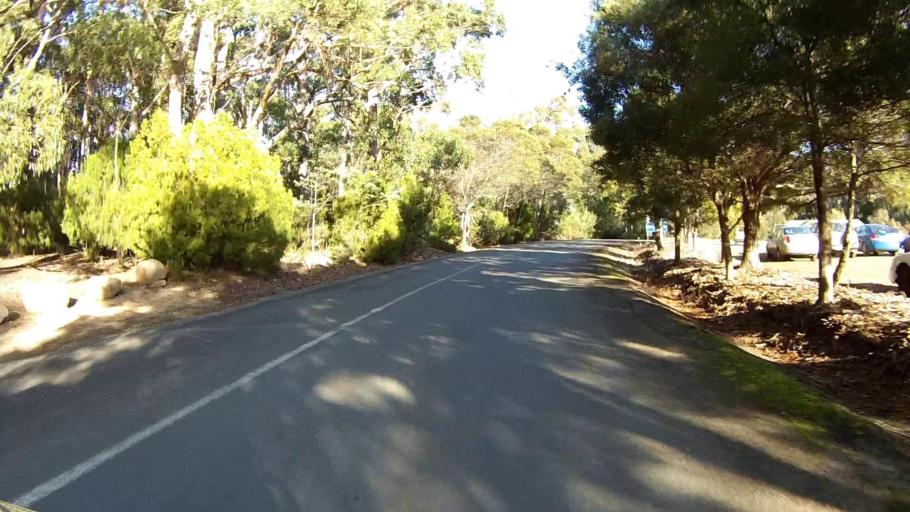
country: AU
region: Tasmania
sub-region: Clarence
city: Sandford
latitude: -43.1447
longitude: 147.8524
